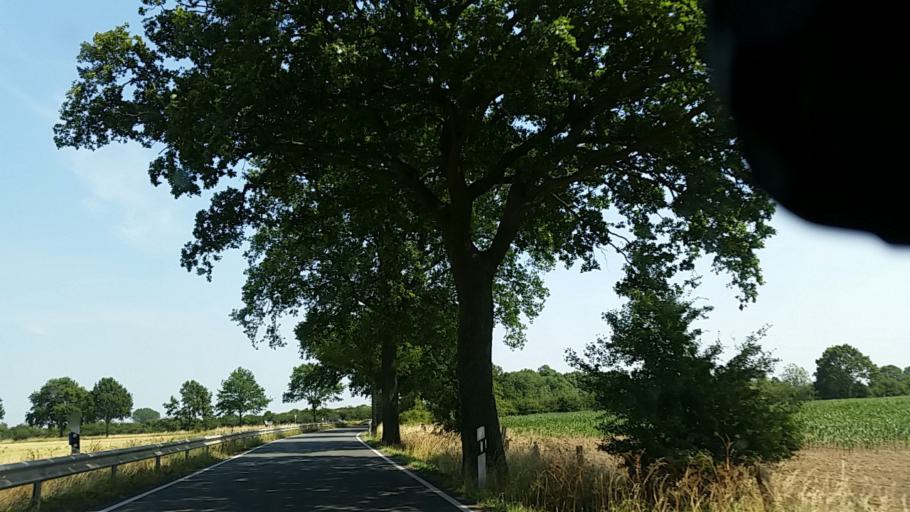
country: DE
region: Lower Saxony
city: Thedinghausen
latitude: 52.9842
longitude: 9.0051
